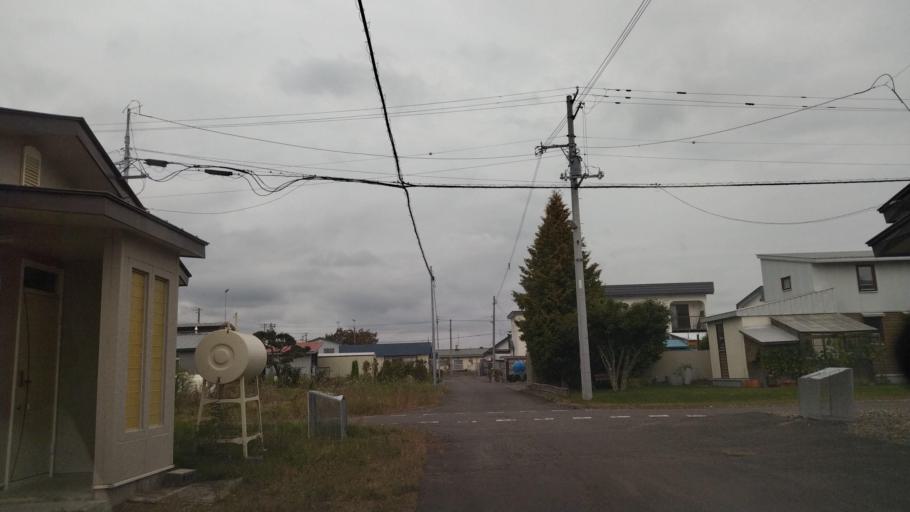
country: JP
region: Hokkaido
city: Otofuke
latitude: 43.2345
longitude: 143.2890
